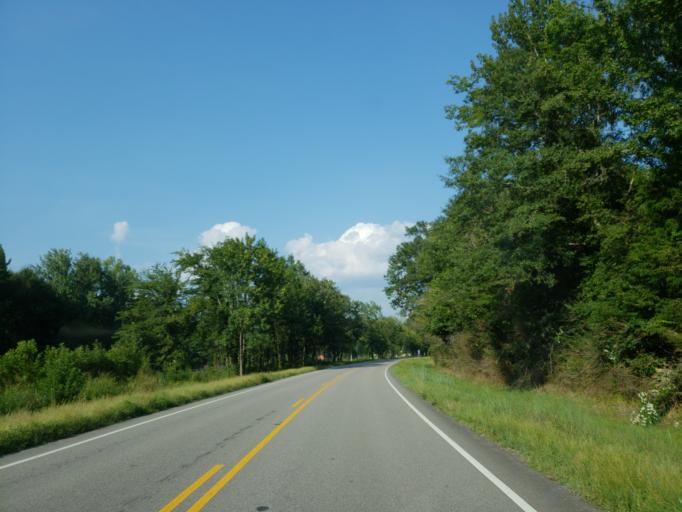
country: US
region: Alabama
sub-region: Greene County
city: Eutaw
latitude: 32.7536
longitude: -88.0335
